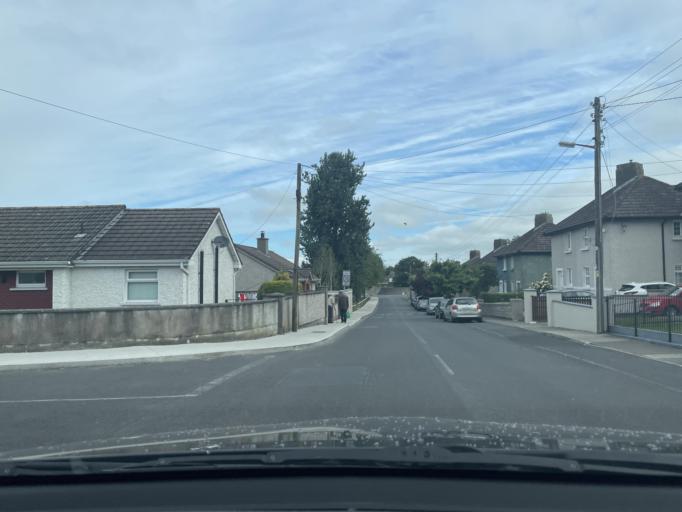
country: IE
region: Leinster
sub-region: County Carlow
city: Bagenalstown
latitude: 52.6992
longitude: -6.9637
